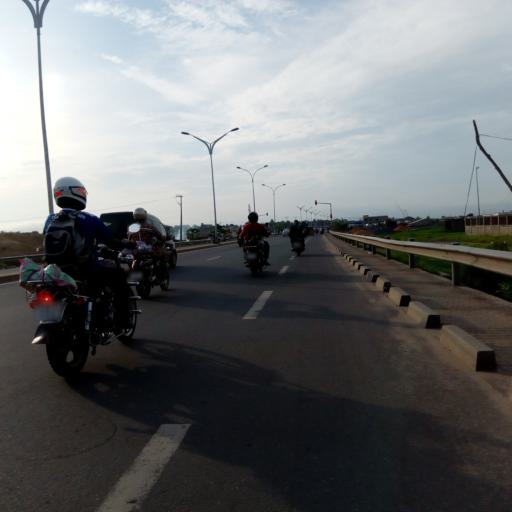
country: TG
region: Maritime
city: Lome
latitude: 6.1895
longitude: 1.2745
